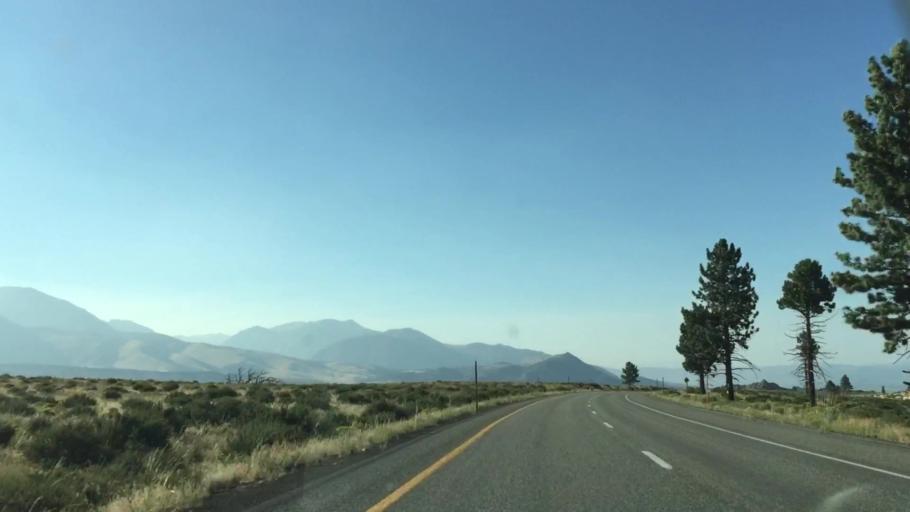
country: US
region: California
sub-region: Mono County
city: Mammoth Lakes
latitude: 37.8314
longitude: -119.0684
